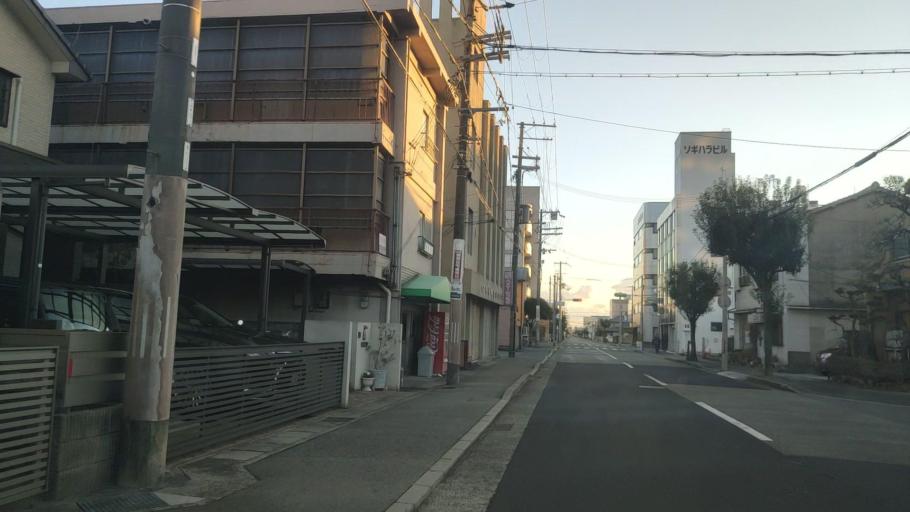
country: JP
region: Hyogo
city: Himeji
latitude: 34.8234
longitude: 134.6845
